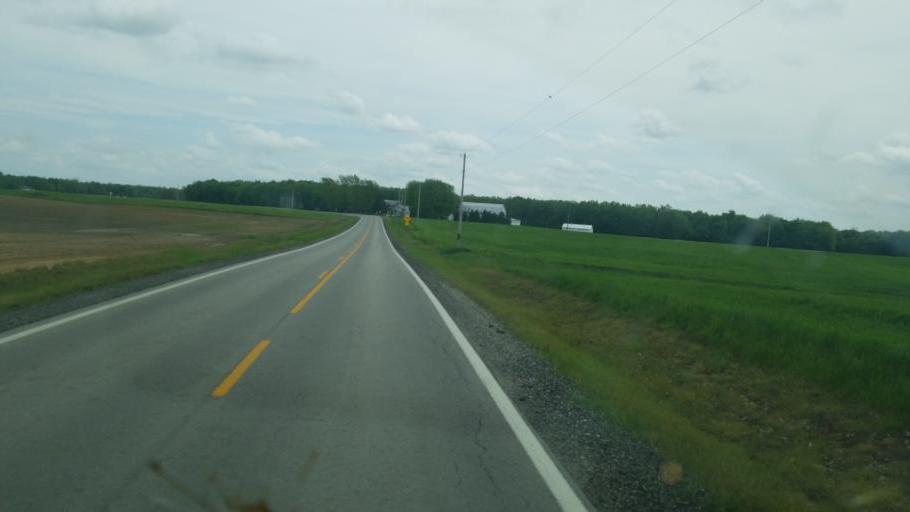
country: US
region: Ohio
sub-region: Crawford County
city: Bucyrus
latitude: 40.9238
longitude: -83.0481
